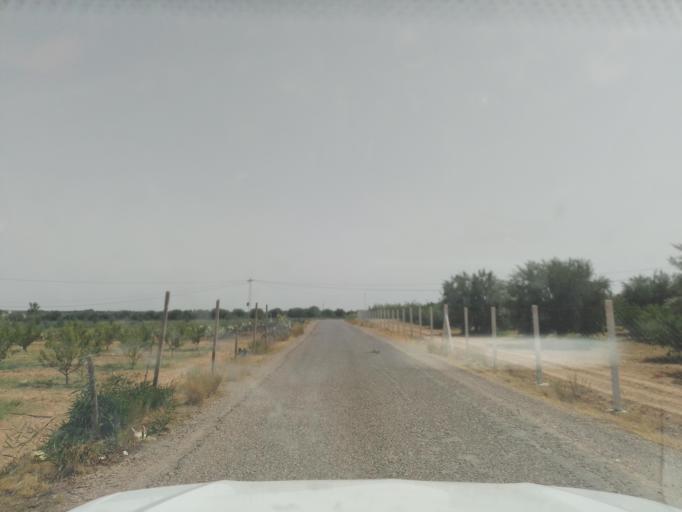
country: TN
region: Al Qasrayn
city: Kasserine
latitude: 35.2652
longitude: 9.0060
